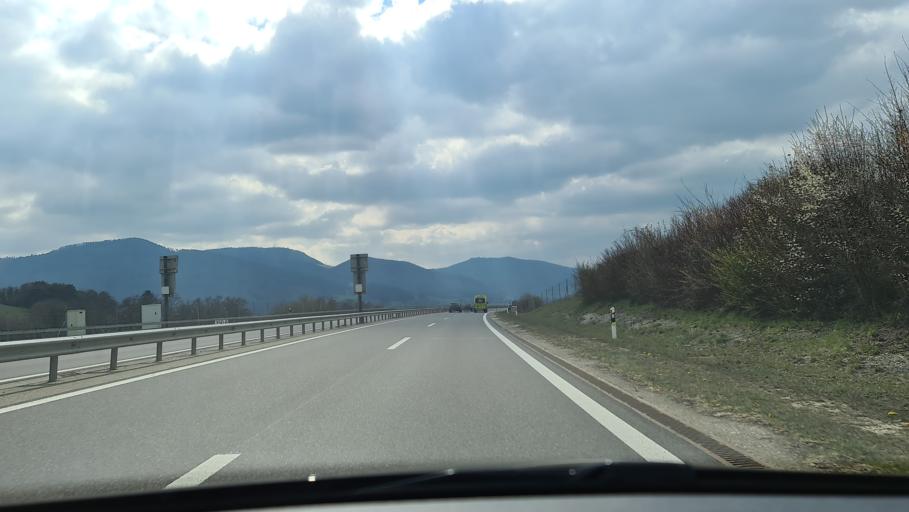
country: CH
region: Jura
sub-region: Delemont District
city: Courfaivre
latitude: 47.3464
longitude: 7.2834
